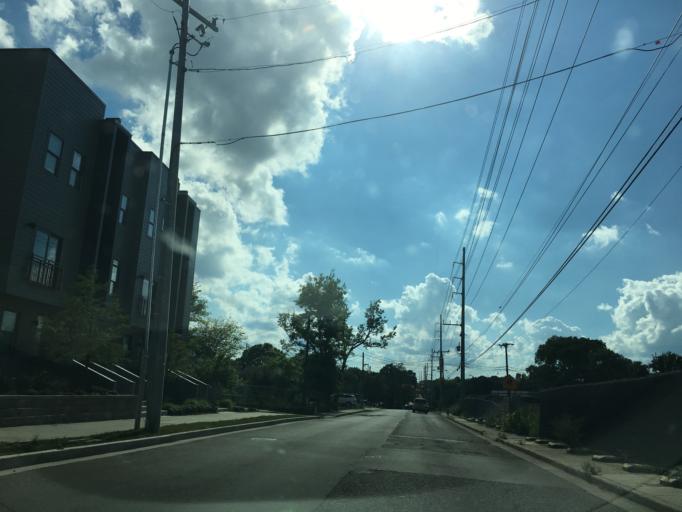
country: US
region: Tennessee
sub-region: Davidson County
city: Nashville
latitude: 36.1586
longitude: -86.8167
